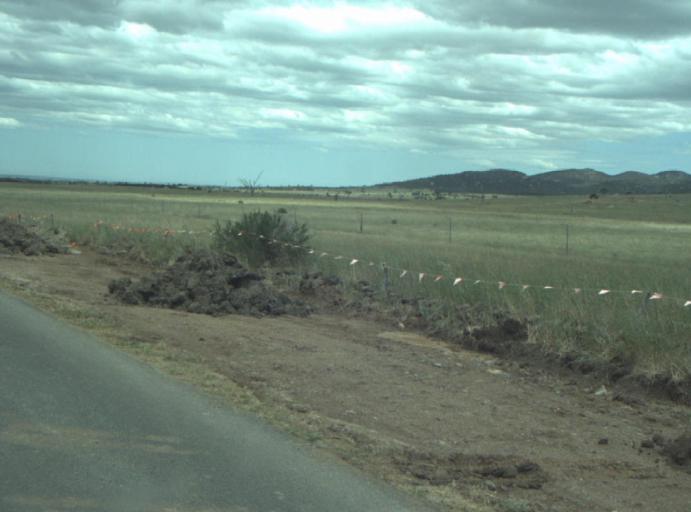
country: AU
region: Victoria
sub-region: Wyndham
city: Little River
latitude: -37.8900
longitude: 144.4610
